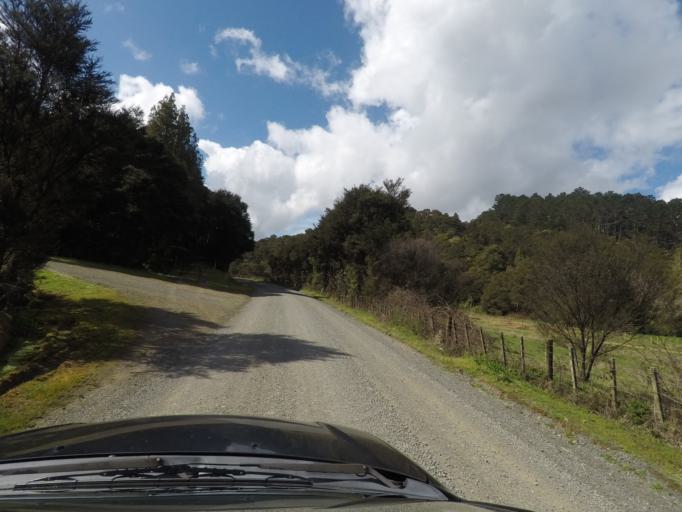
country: NZ
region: Auckland
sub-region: Auckland
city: Red Hill
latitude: -37.0935
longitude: 175.1529
